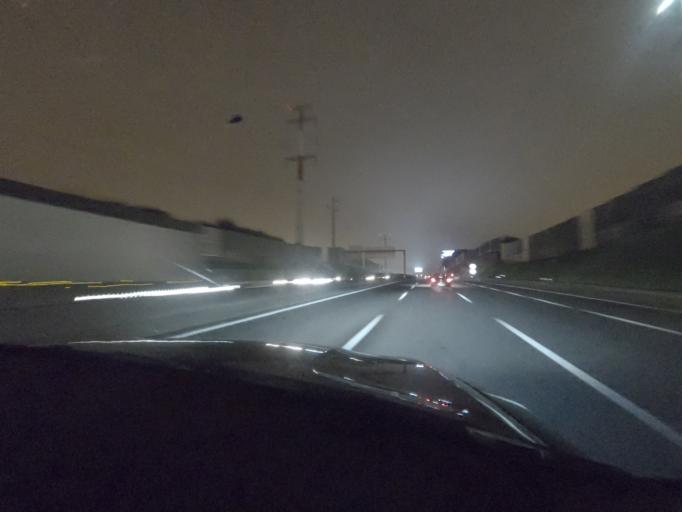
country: PT
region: Lisbon
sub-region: Loures
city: Santa Iria da Azoia
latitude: 38.8451
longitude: -9.0917
